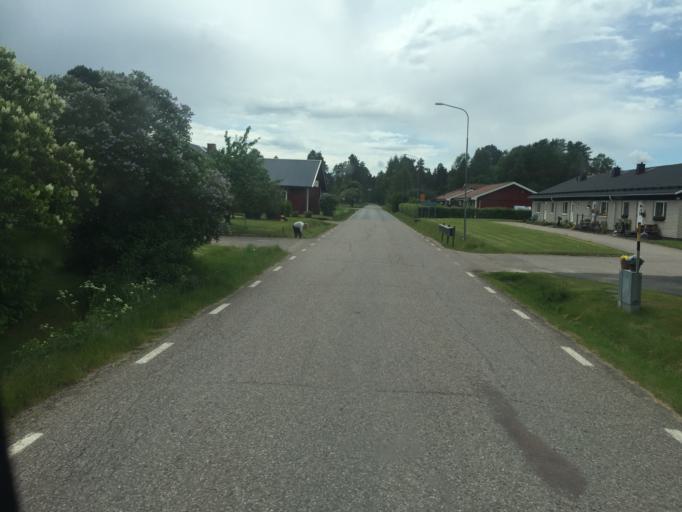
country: SE
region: Dalarna
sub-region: Vansbro Kommun
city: Vansbro
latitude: 60.4828
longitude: 14.0102
